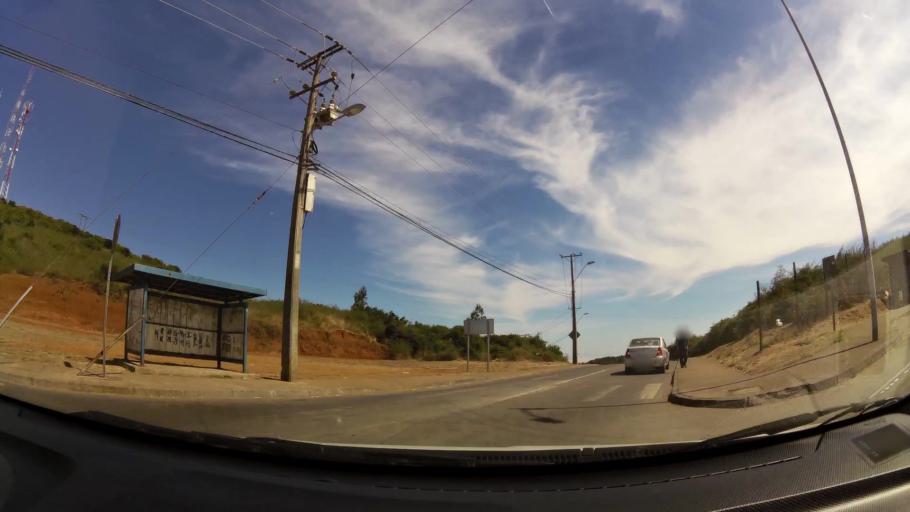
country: CL
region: Biobio
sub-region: Provincia de Concepcion
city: Talcahuano
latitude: -36.7104
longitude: -73.1255
